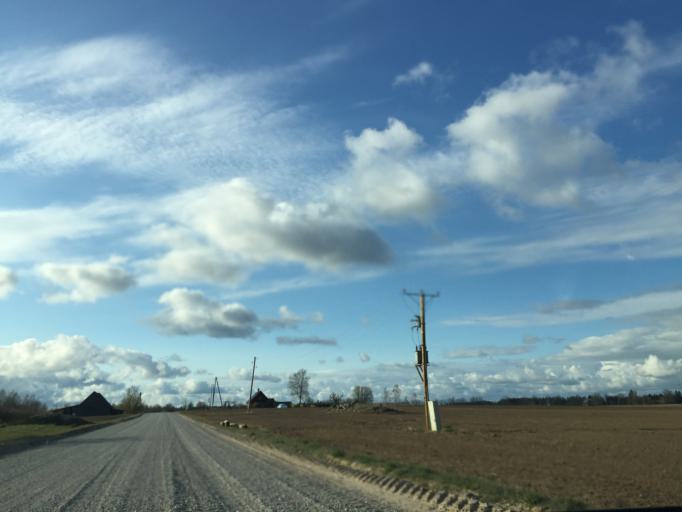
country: LV
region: Burtnieki
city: Matisi
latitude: 57.6282
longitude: 25.0575
